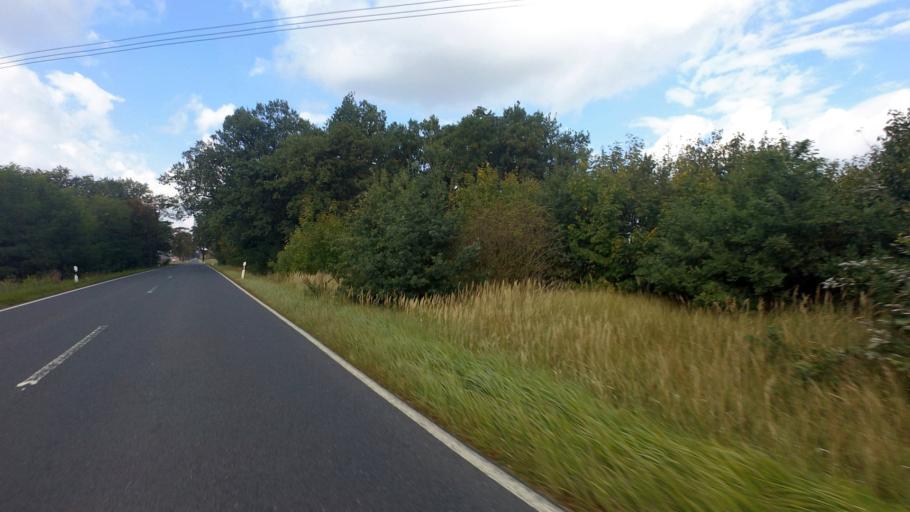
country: DE
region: Saxony-Anhalt
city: Holzdorf
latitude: 51.8299
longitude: 13.1577
